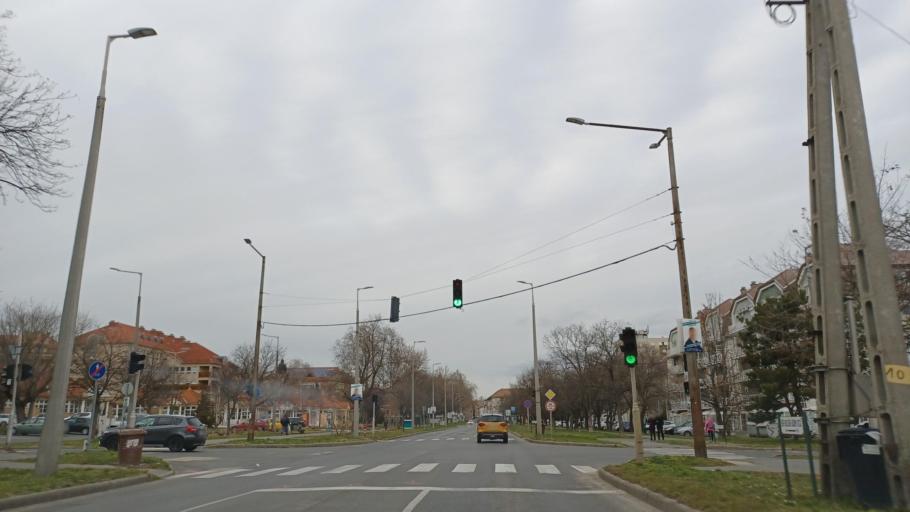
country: HU
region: Tolna
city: Szekszard
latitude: 46.3416
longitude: 18.7011
